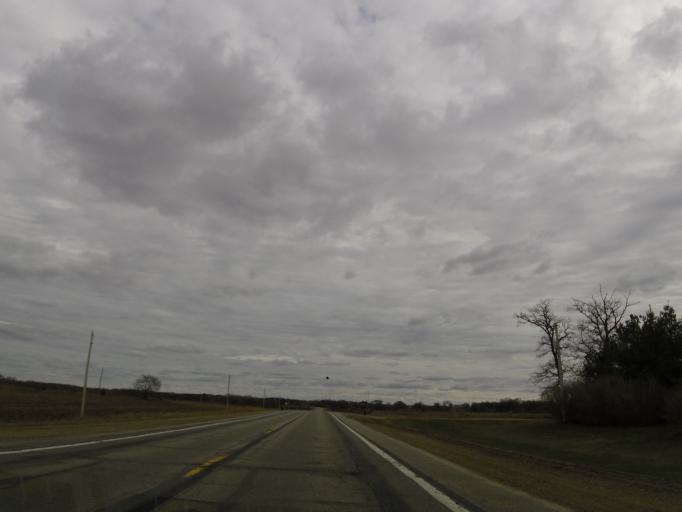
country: US
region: Iowa
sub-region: Howard County
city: Cresco
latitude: 43.4694
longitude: -92.3181
